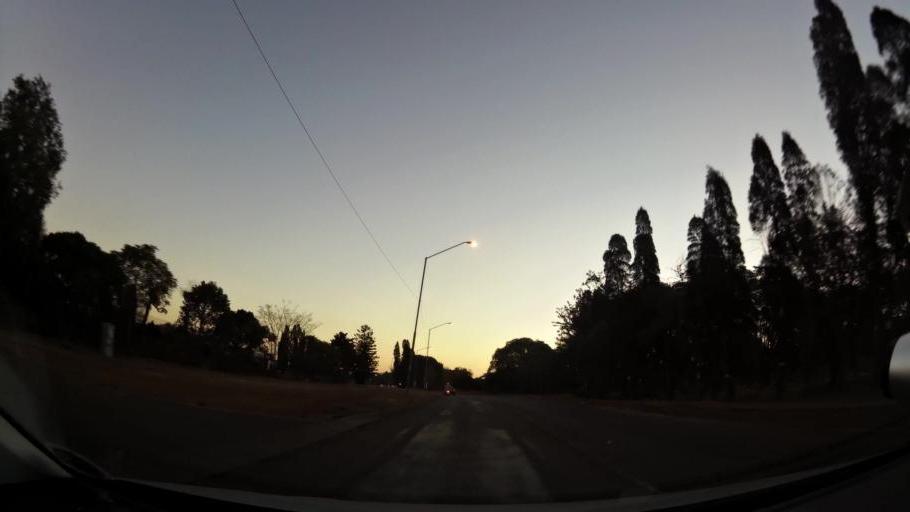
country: ZA
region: Gauteng
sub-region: City of Tshwane Metropolitan Municipality
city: Pretoria
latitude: -25.7391
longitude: 28.1556
